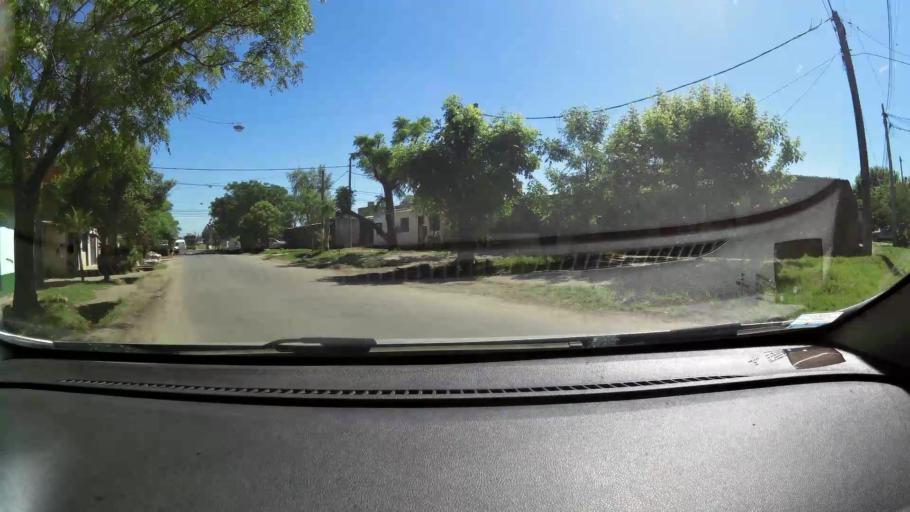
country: AR
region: Santa Fe
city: Perez
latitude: -32.9732
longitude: -60.7055
